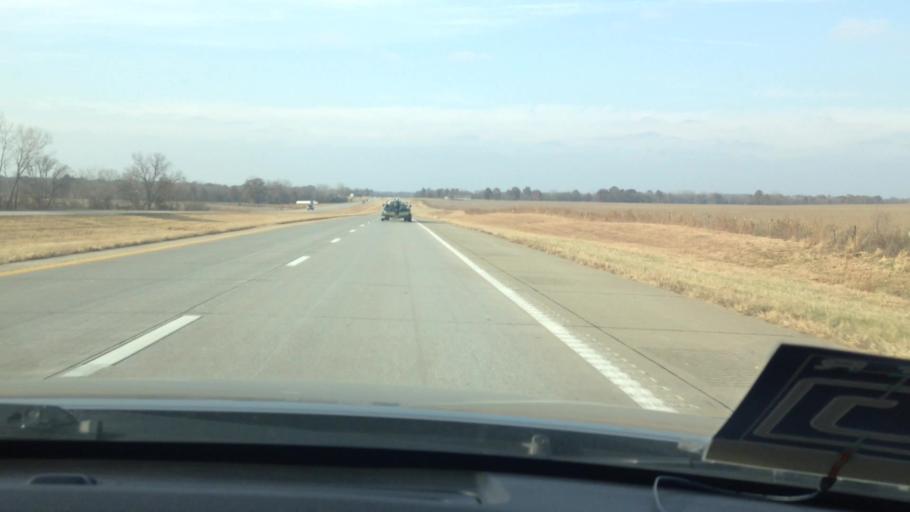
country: US
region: Missouri
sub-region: Henry County
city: Clinton
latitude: 38.4461
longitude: -93.9563
